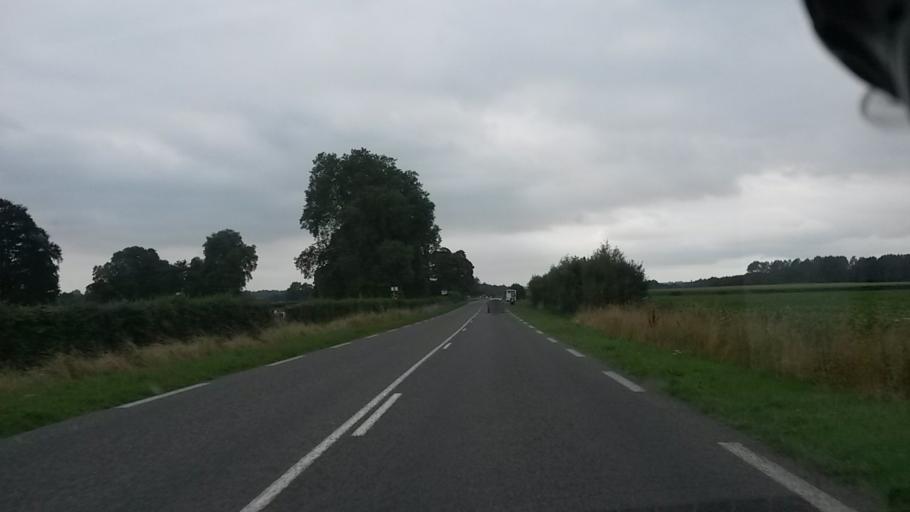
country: FR
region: Haute-Normandie
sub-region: Departement de la Seine-Maritime
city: Aumale
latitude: 49.7666
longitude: 1.7945
